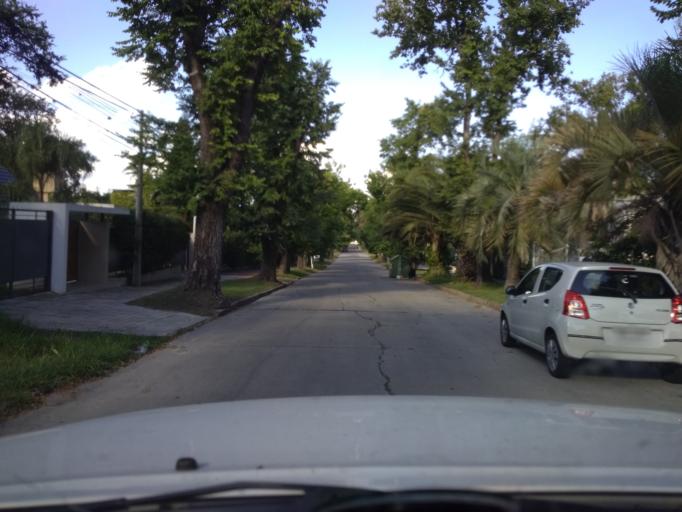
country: UY
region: Canelones
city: Paso de Carrasco
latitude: -34.8877
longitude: -56.0772
